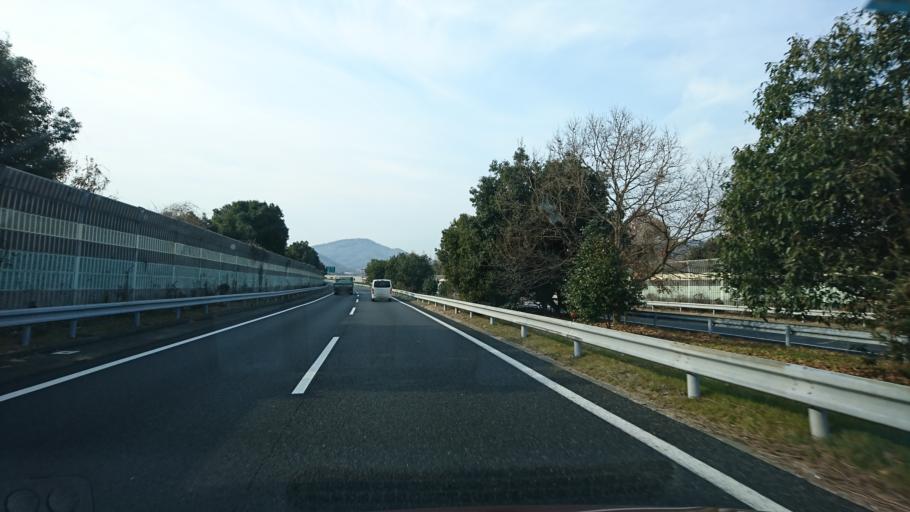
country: JP
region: Okayama
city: Okayama-shi
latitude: 34.7515
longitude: 134.0354
